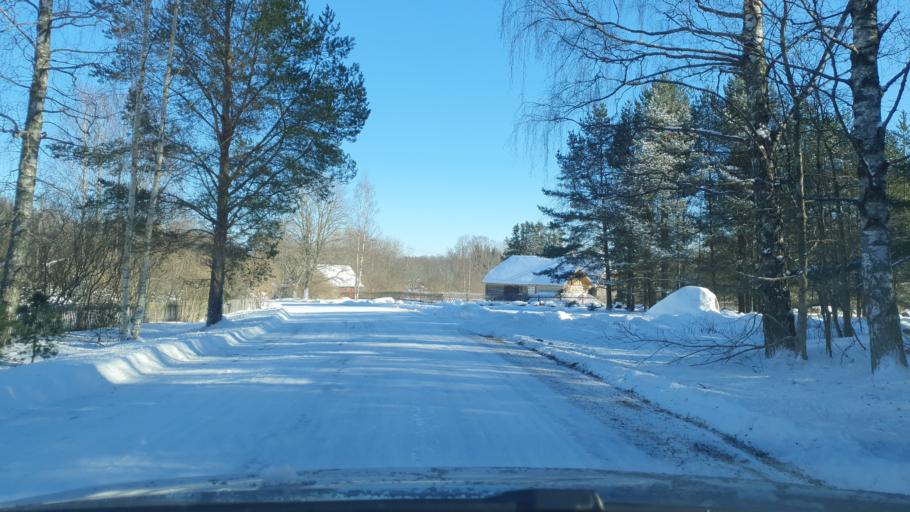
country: EE
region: Harju
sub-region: Loksa linn
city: Loksa
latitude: 59.6080
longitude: 25.9943
